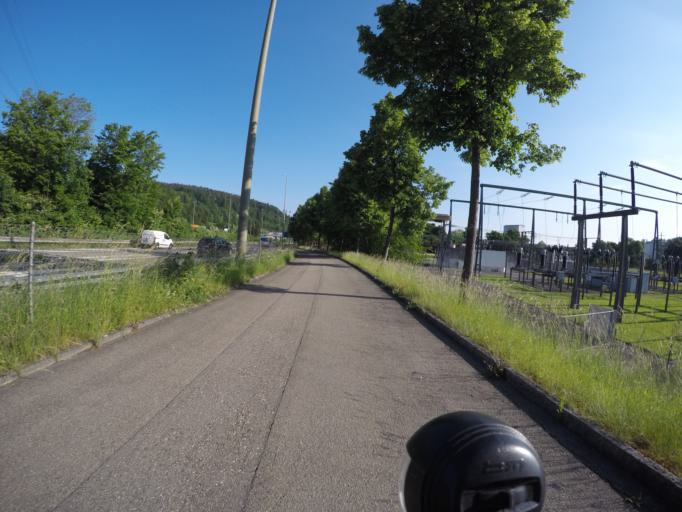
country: CH
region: Zurich
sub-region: Bezirk Winterthur
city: Toss
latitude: 47.4803
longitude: 8.7051
